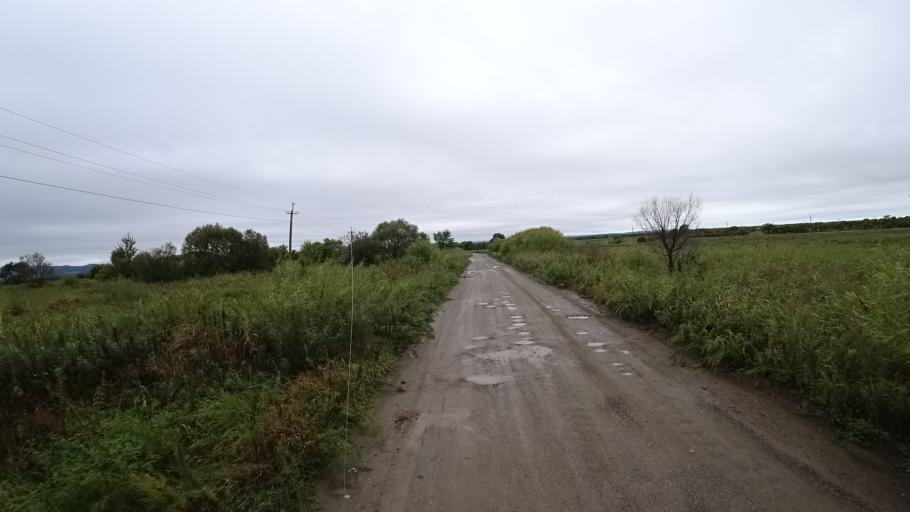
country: RU
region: Primorskiy
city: Monastyrishche
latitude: 44.2309
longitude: 132.4582
